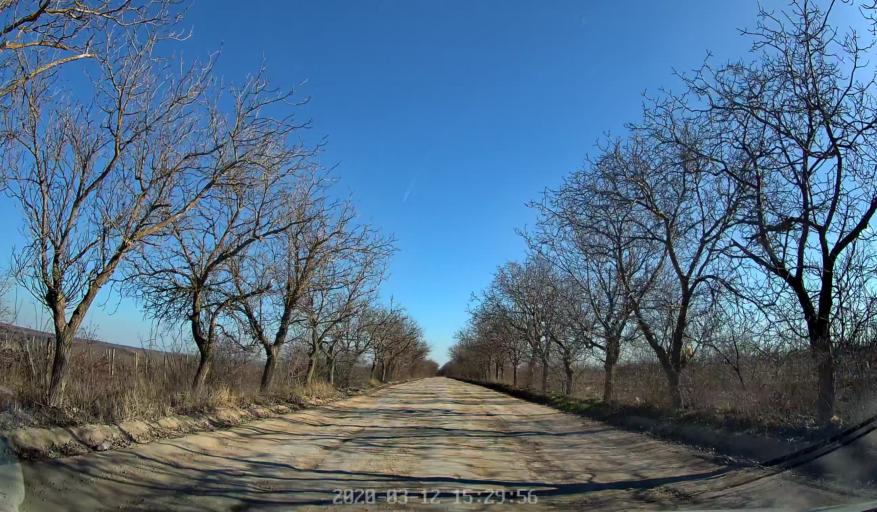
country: MD
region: Chisinau
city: Ciorescu
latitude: 47.1627
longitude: 28.9371
